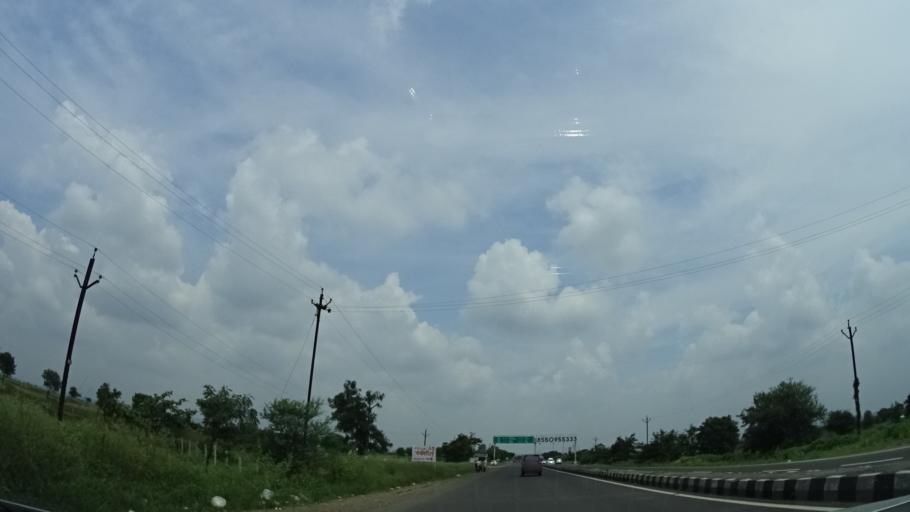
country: IN
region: Maharashtra
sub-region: Pune Division
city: Sirur
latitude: 18.9348
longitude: 74.4954
